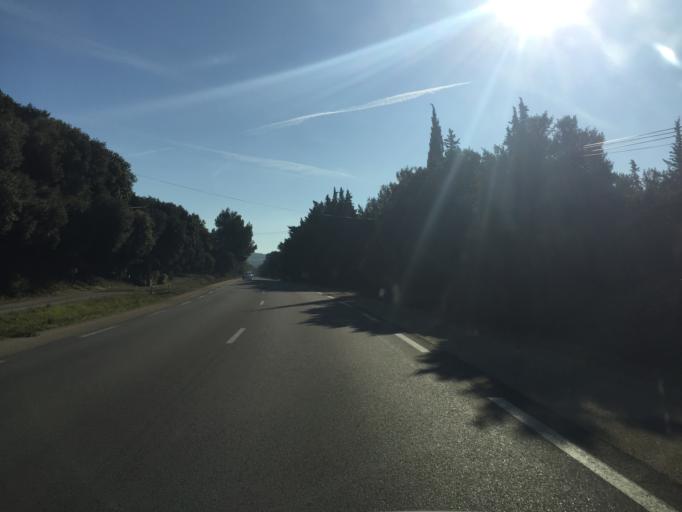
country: FR
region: Provence-Alpes-Cote d'Azur
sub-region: Departement des Bouches-du-Rhone
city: Orgon
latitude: 43.8013
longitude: 5.0268
